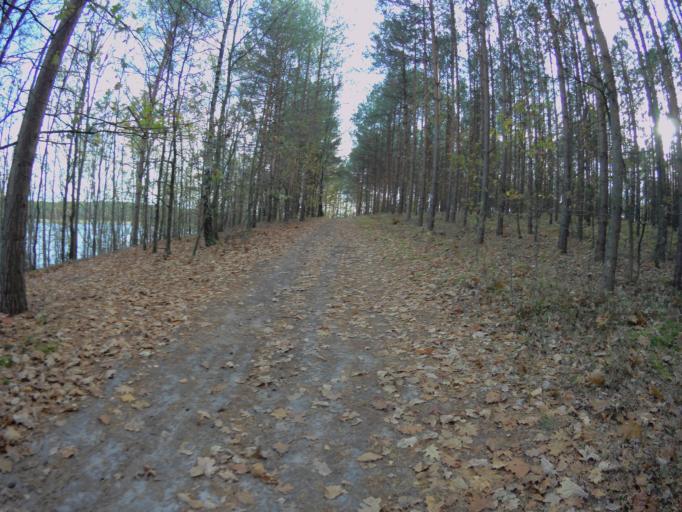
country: PL
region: Subcarpathian Voivodeship
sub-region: Powiat kolbuszowski
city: Lipnica
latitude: 50.3355
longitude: 21.9375
